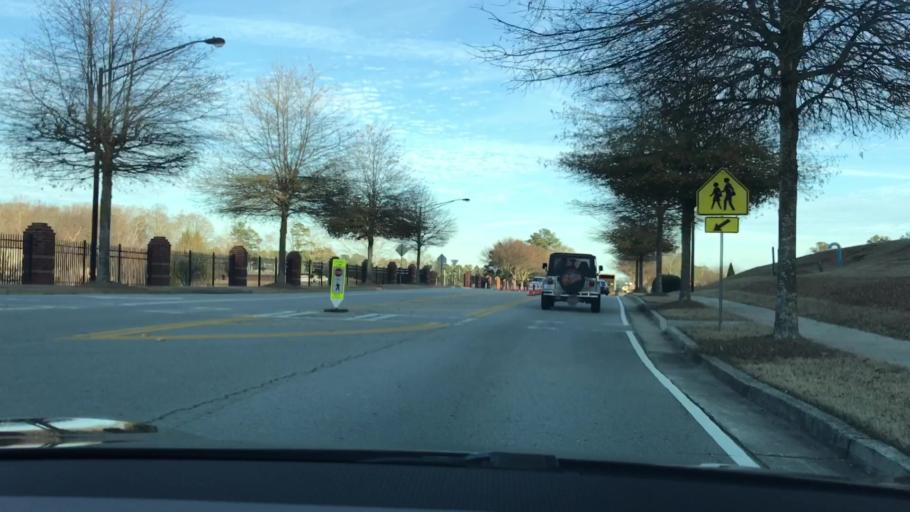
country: US
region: Georgia
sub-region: Gwinnett County
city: Buford
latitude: 34.1338
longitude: -83.9965
